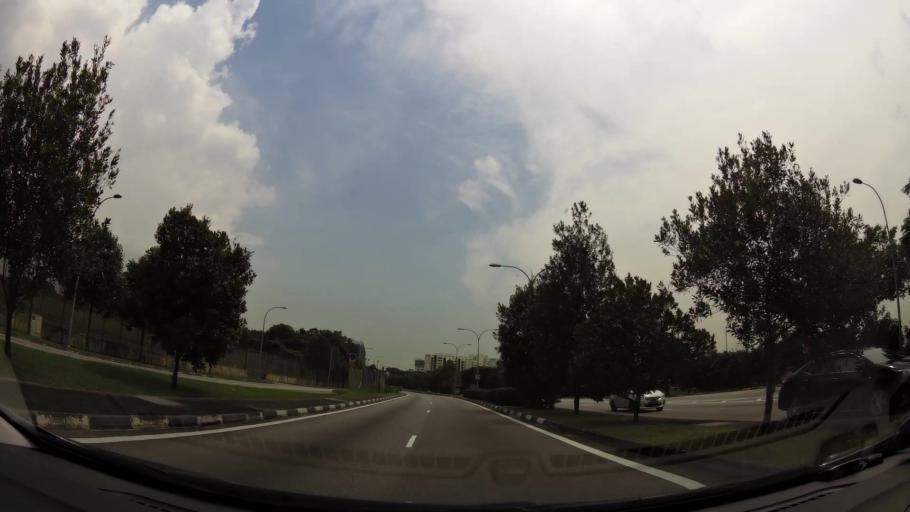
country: SG
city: Singapore
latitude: 1.3392
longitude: 103.9002
